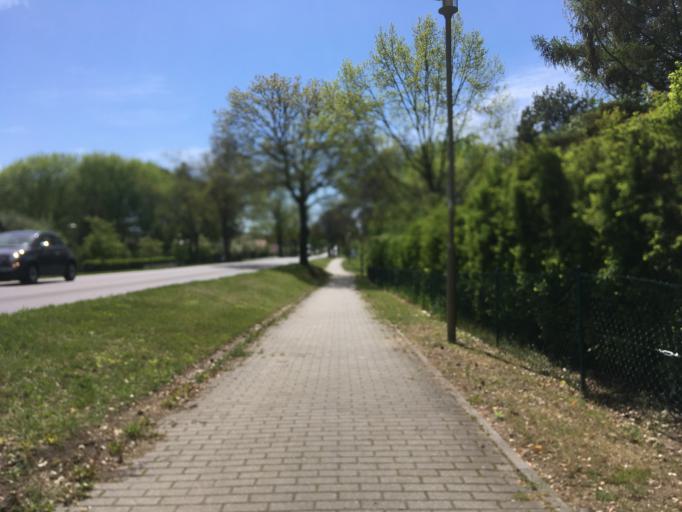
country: DE
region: Brandenburg
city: Zeuthen
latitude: 52.3369
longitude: 13.6085
